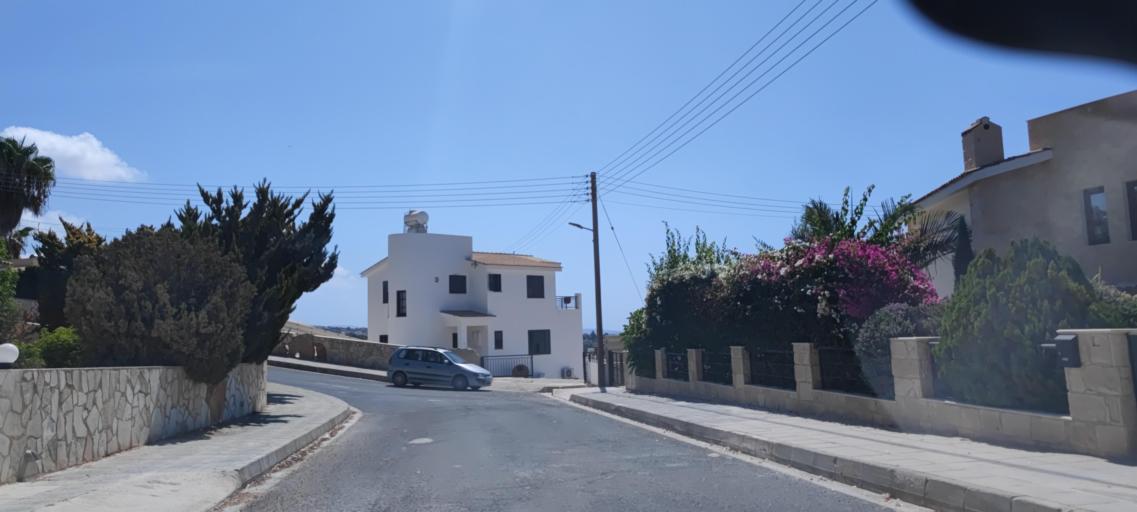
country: CY
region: Pafos
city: Pegeia
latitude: 34.8856
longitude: 32.3315
